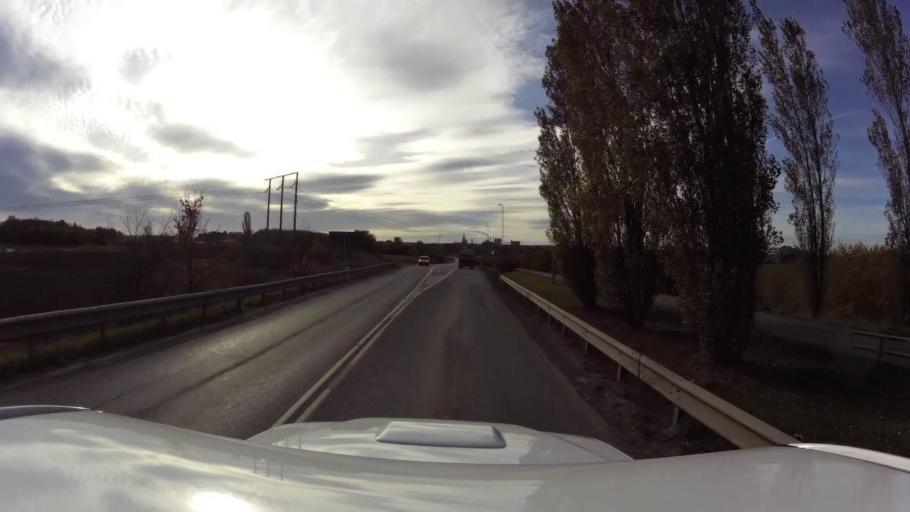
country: SE
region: OEstergoetland
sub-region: Linkopings Kommun
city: Linkoping
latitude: 58.4323
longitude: 15.6436
